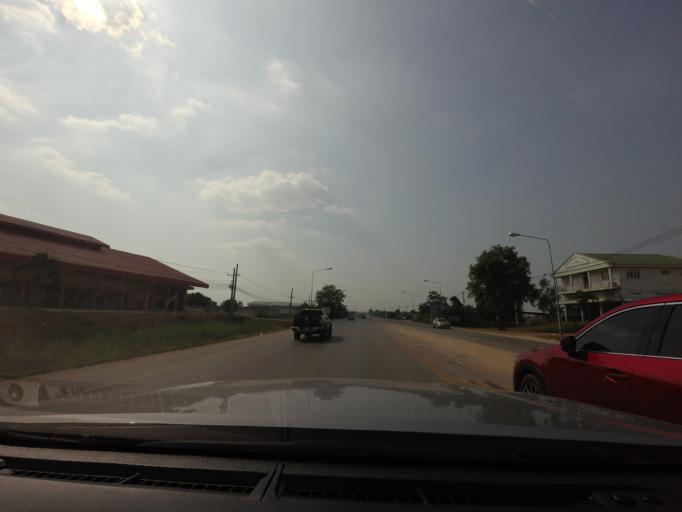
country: TH
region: Phitsanulok
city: Bang Rakam
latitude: 16.7461
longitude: 100.1095
